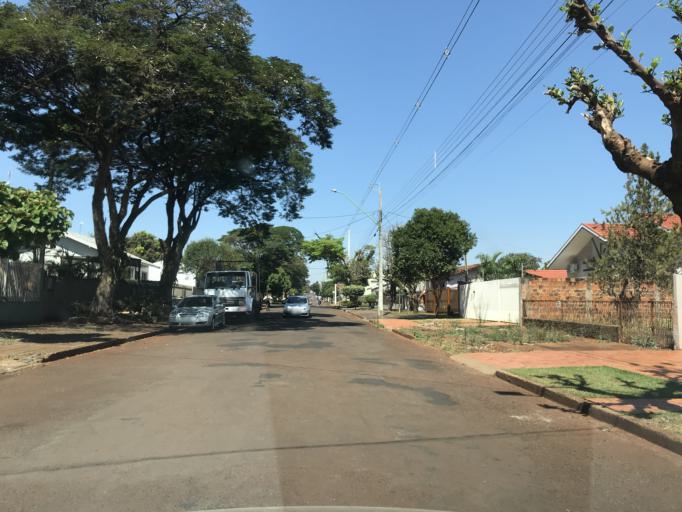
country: BR
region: Parana
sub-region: Palotina
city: Palotina
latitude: -24.2791
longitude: -53.8450
